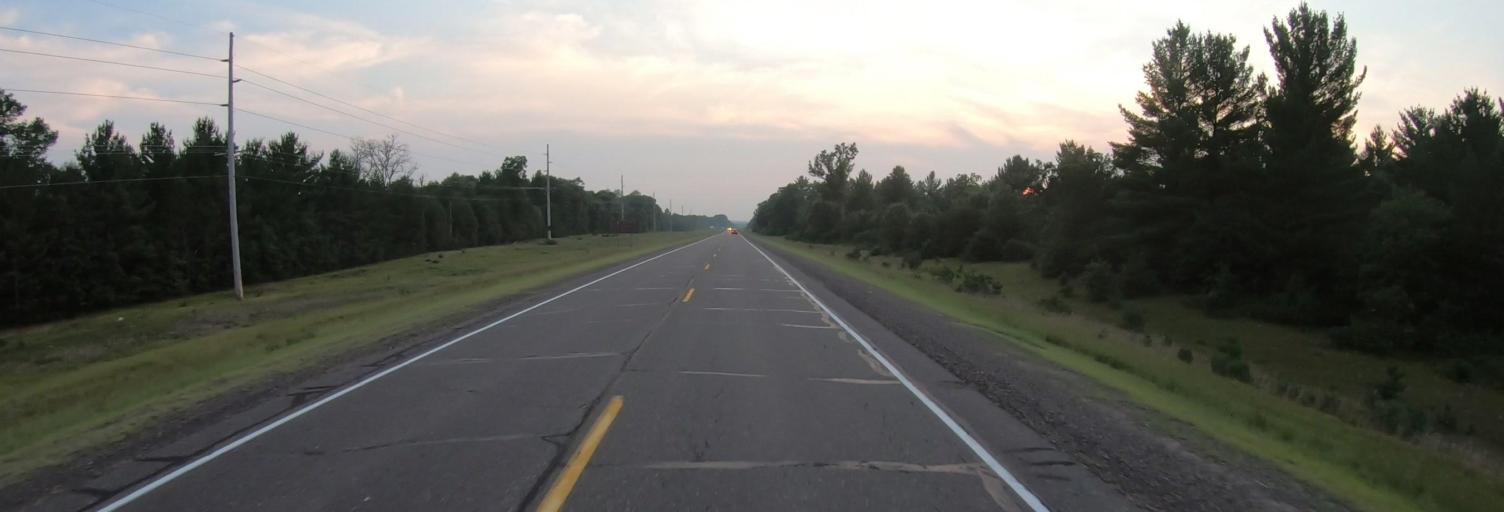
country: US
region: Wisconsin
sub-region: Burnett County
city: Grantsburg
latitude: 45.7731
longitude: -92.7476
